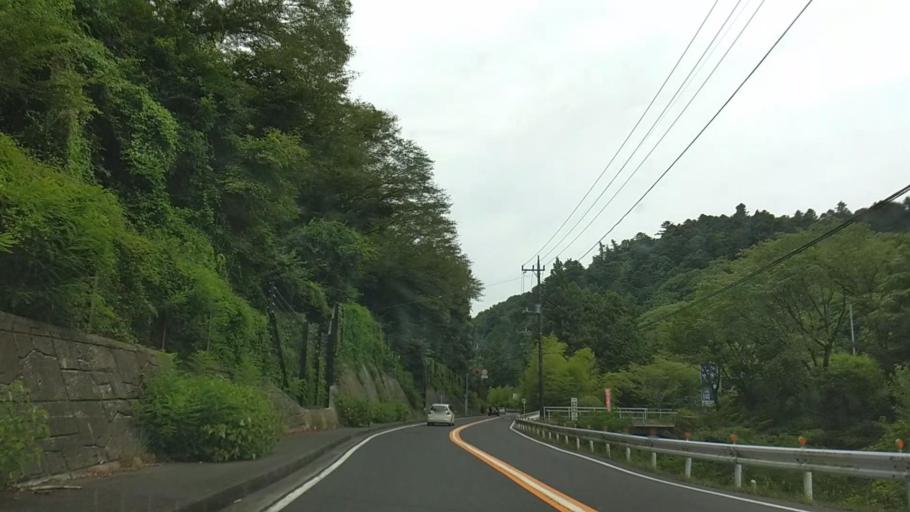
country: JP
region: Tokyo
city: Hachioji
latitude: 35.6161
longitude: 139.2416
